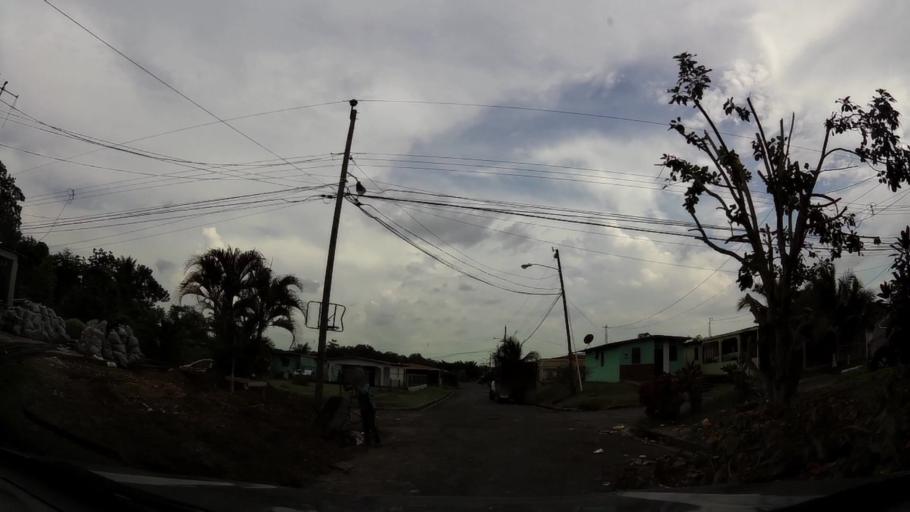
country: PA
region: Panama
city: Cabra Numero Uno
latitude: 9.0983
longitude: -79.3453
